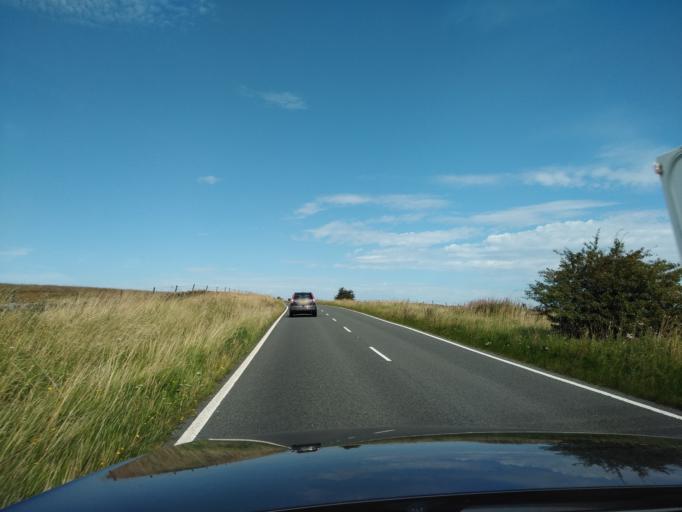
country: GB
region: England
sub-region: Derbyshire
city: Hathersage
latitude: 53.3036
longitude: -1.5927
